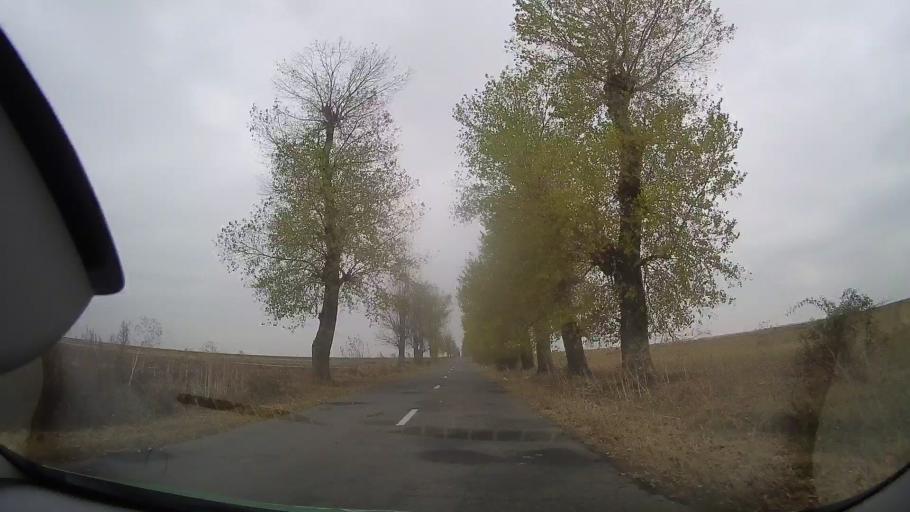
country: RO
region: Ialomita
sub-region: Comuna Grindu
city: Grindu
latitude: 44.7620
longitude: 26.8787
